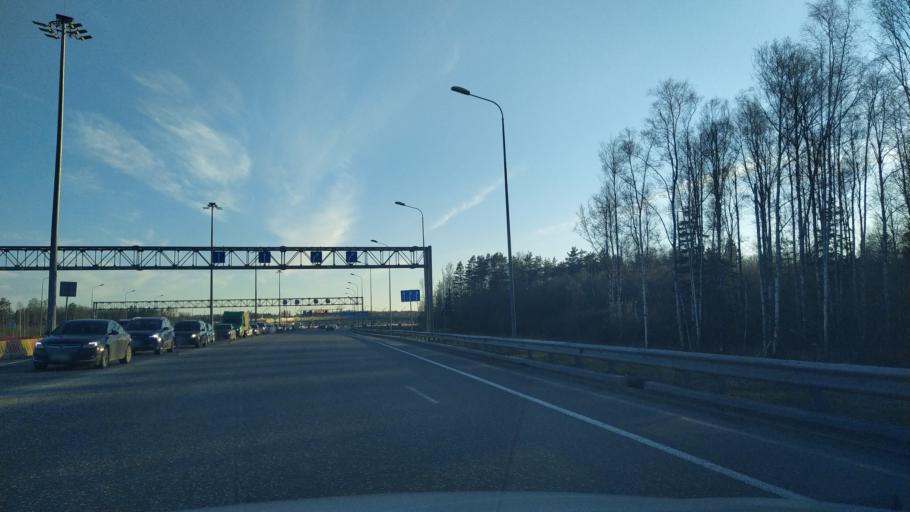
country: RU
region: St.-Petersburg
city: Pesochnyy
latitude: 60.0631
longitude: 30.1608
